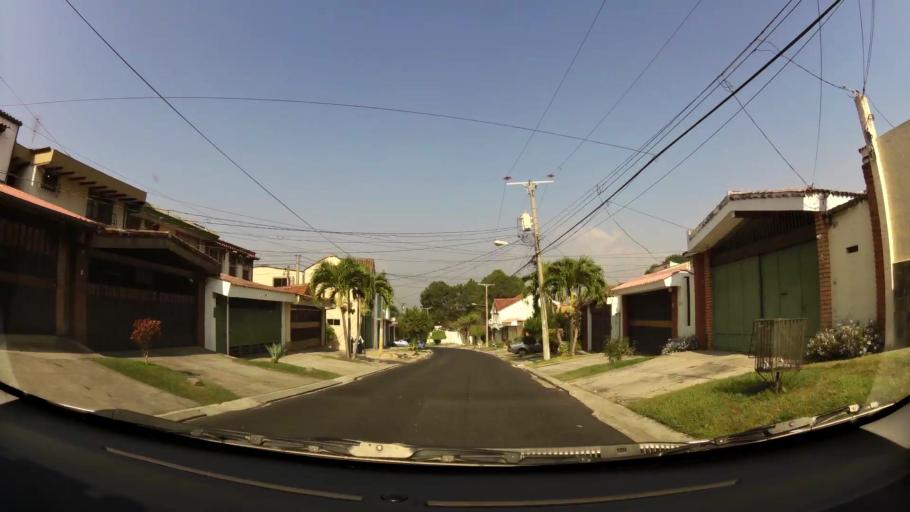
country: SV
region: La Libertad
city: Antiguo Cuscatlan
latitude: 13.6688
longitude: -89.2292
